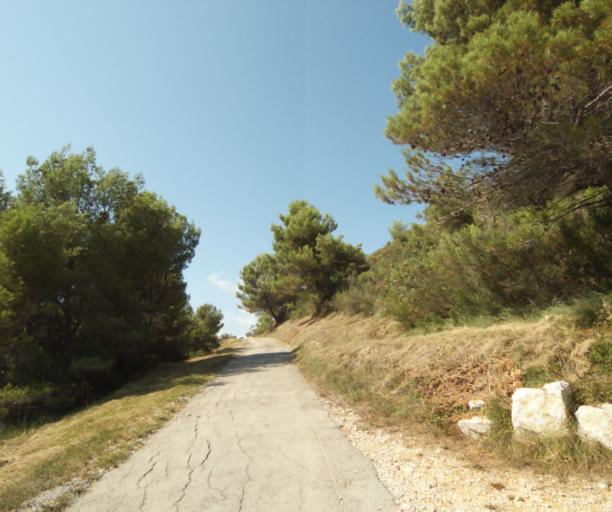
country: FR
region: Provence-Alpes-Cote d'Azur
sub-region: Departement des Alpes-Maritimes
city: Drap
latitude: 43.7548
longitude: 7.3507
